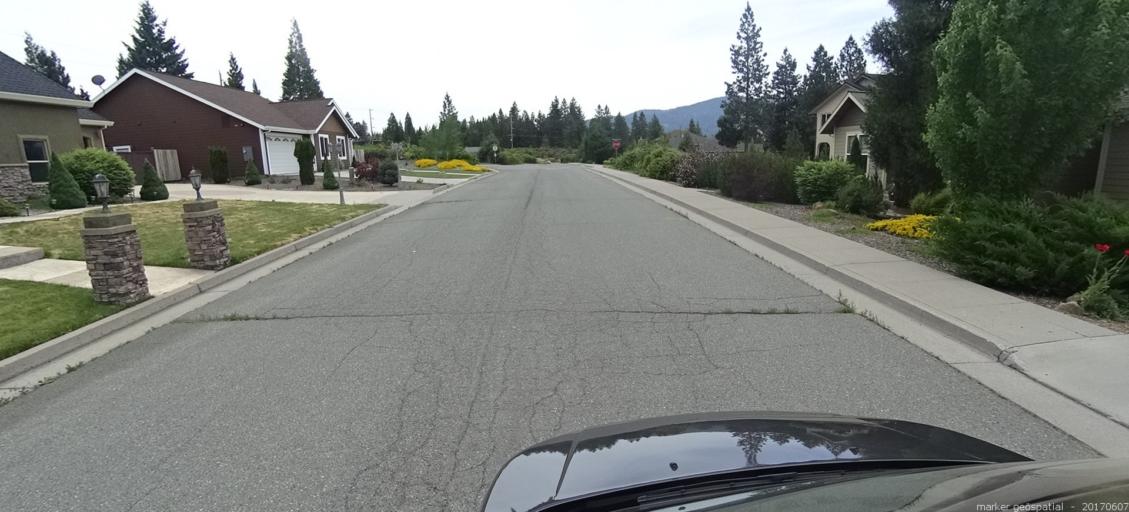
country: US
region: California
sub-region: Siskiyou County
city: Mount Shasta
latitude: 41.2932
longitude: -122.3133
